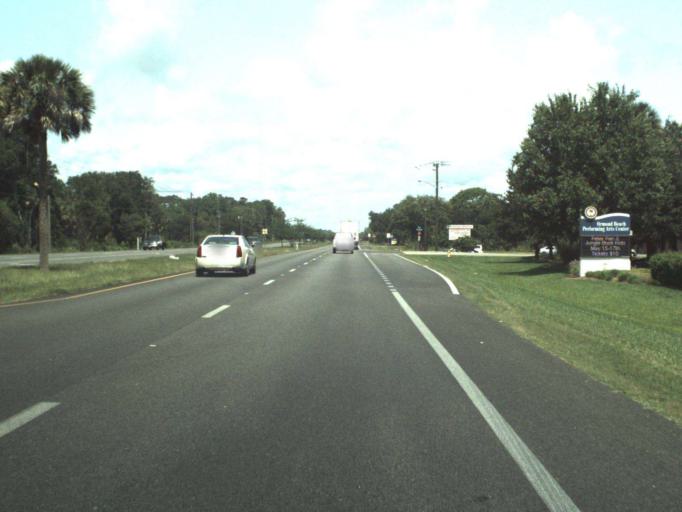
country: US
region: Florida
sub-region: Volusia County
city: Ormond Beach
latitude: 29.2908
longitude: -81.0698
